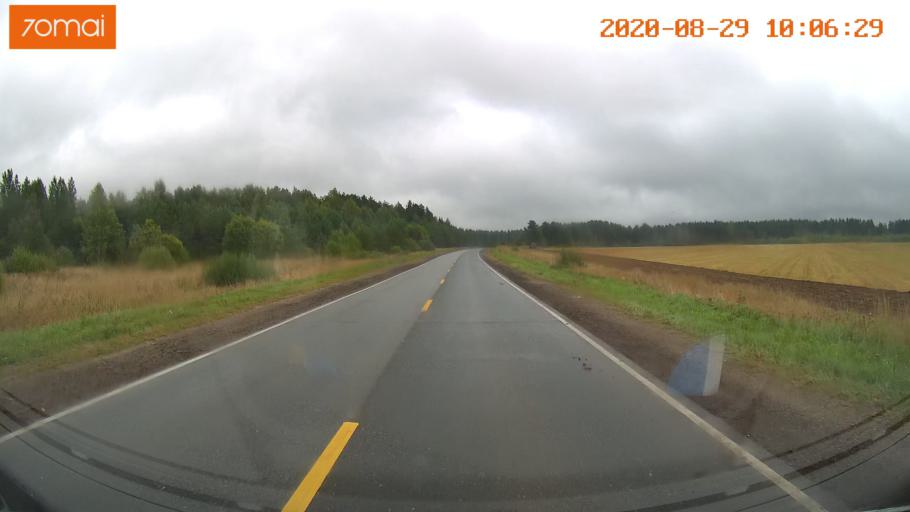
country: RU
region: Ivanovo
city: Kuznechikha
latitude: 57.3883
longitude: 42.5464
